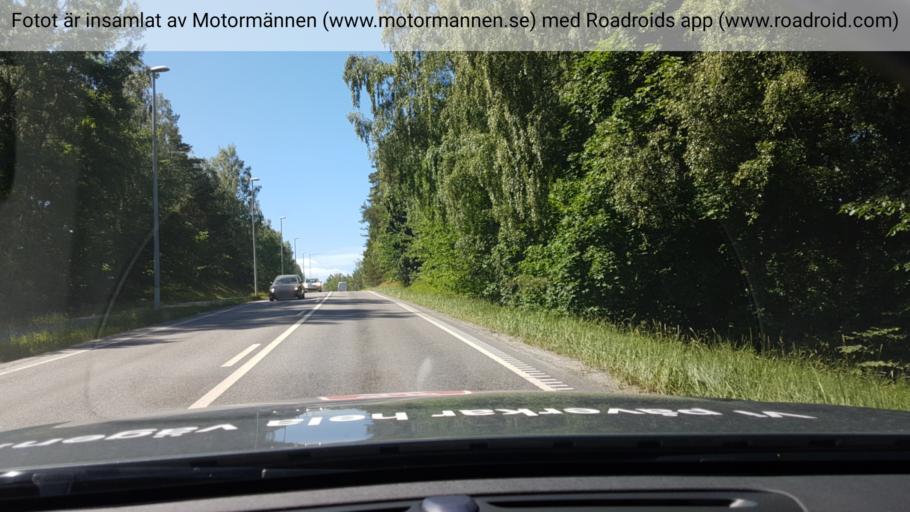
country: SE
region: Stockholm
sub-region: Tyreso Kommun
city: Bollmora
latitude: 59.2019
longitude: 18.1935
